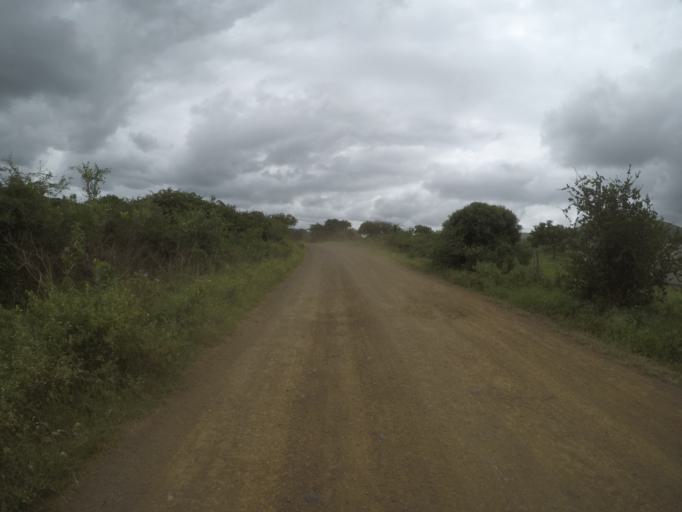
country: ZA
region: KwaZulu-Natal
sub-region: uThungulu District Municipality
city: Empangeni
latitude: -28.5615
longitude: 31.8746
